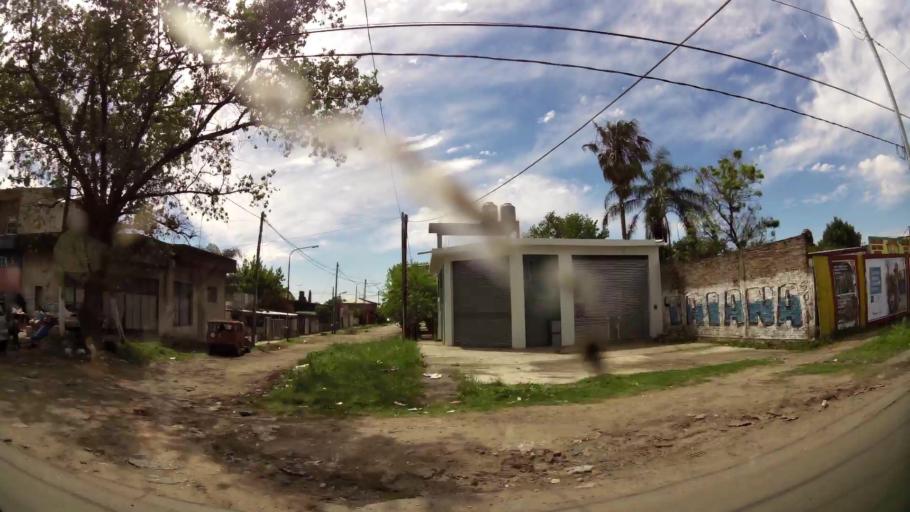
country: AR
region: Buenos Aires
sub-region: Partido de Quilmes
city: Quilmes
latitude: -34.7755
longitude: -58.2838
